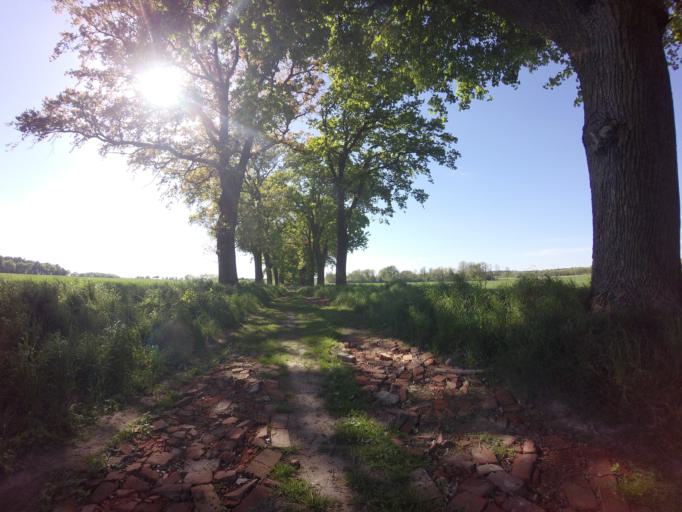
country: PL
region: West Pomeranian Voivodeship
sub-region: Powiat choszczenski
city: Choszczno
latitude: 53.1566
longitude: 15.3169
